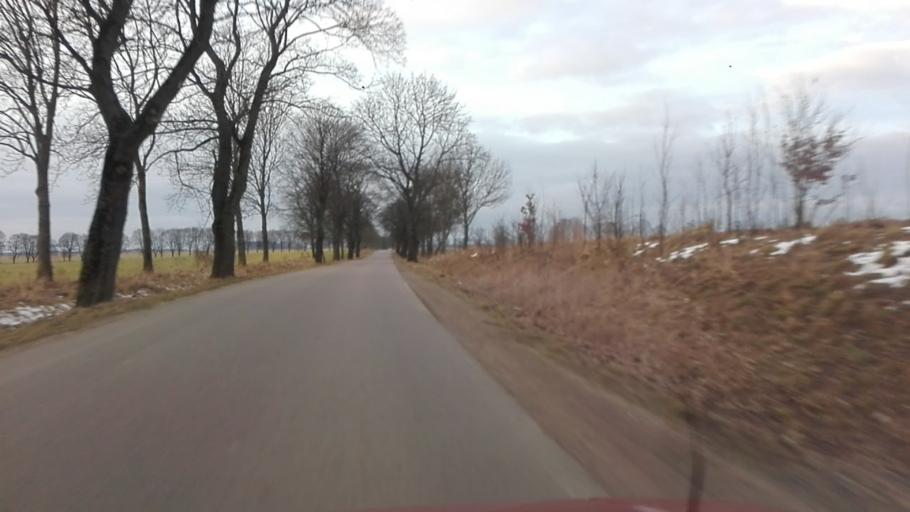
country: PL
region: West Pomeranian Voivodeship
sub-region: Powiat swidwinski
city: Rabino
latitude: 53.8024
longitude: 15.9114
